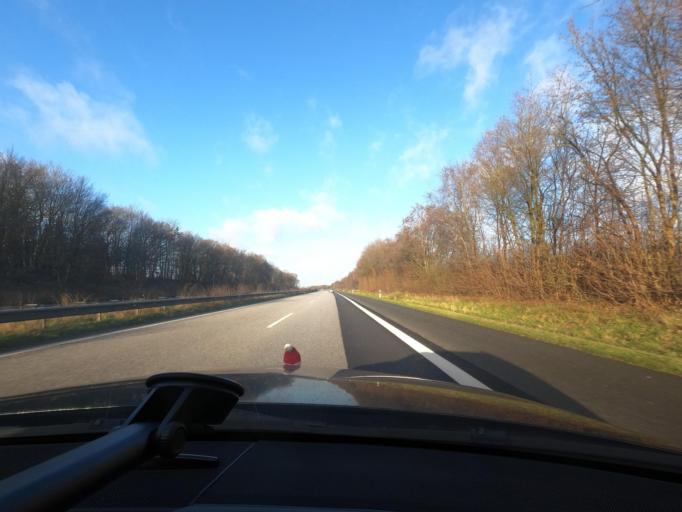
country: DE
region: Schleswig-Holstein
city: Lurschau
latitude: 54.5770
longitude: 9.4687
